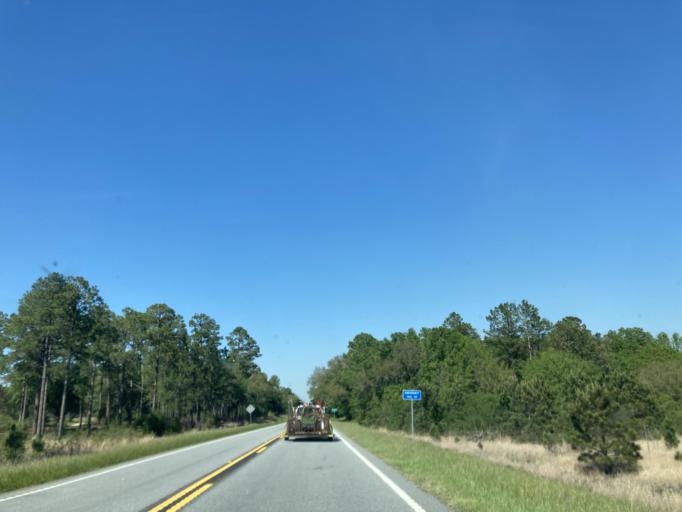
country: US
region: Georgia
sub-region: Baker County
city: Newton
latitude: 31.4365
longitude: -84.2747
